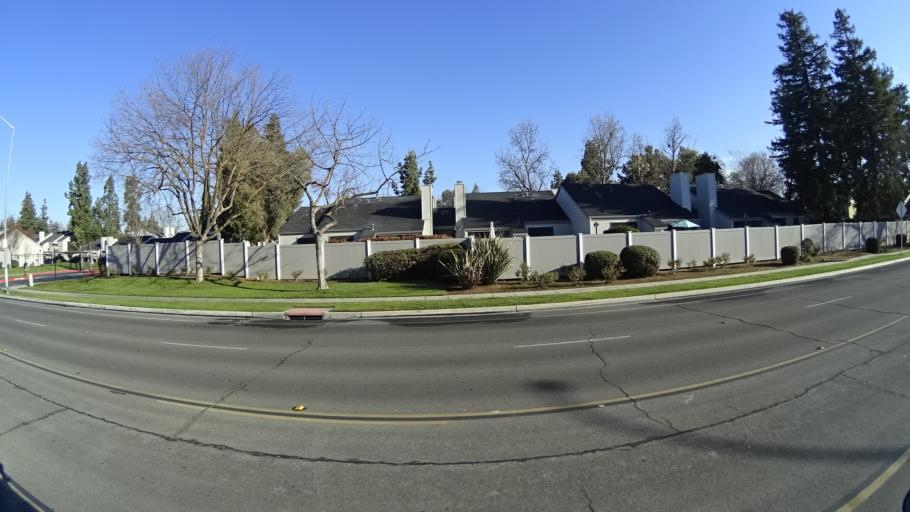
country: US
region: California
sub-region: Fresno County
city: West Park
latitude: 36.8119
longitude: -119.8596
